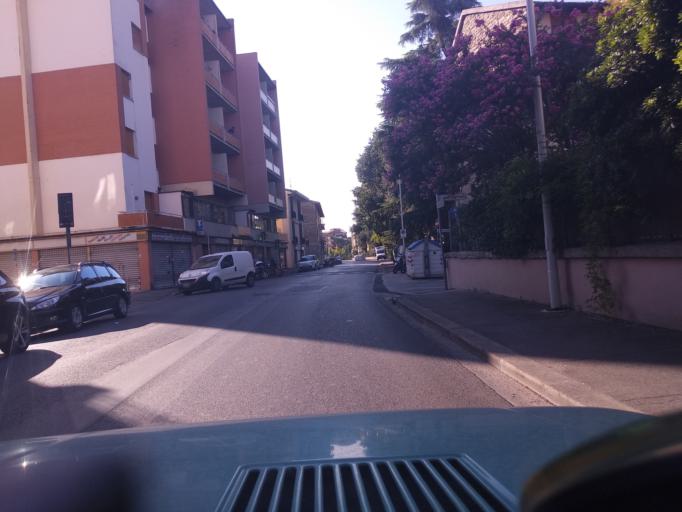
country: IT
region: Tuscany
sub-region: Province of Florence
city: Florence
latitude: 43.7770
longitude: 11.2150
